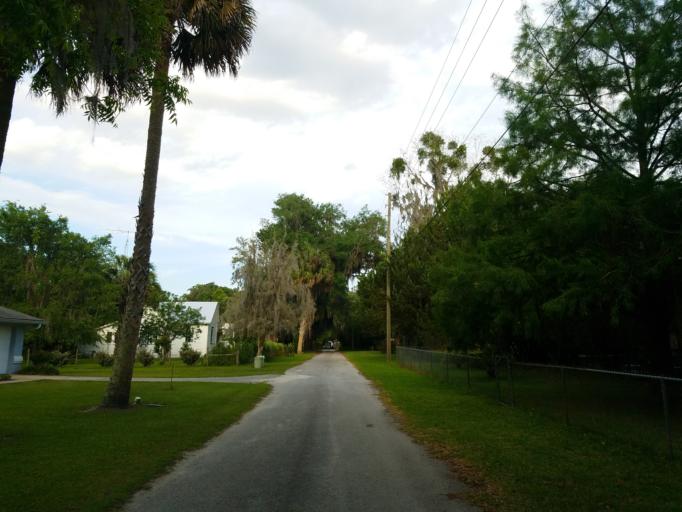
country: US
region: Florida
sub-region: Alachua County
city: Gainesville
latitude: 29.5074
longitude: -82.2813
